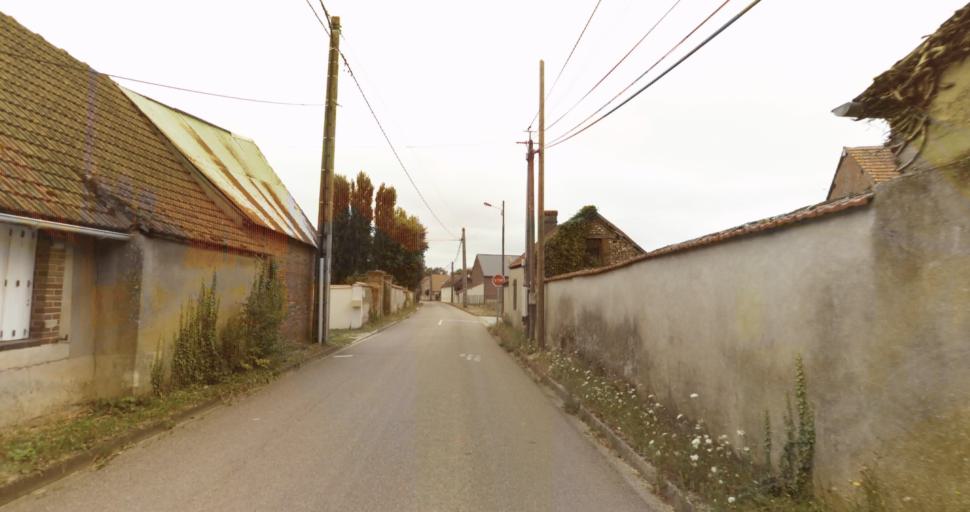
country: FR
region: Haute-Normandie
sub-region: Departement de l'Eure
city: La Couture-Boussey
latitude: 48.9073
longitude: 1.3498
